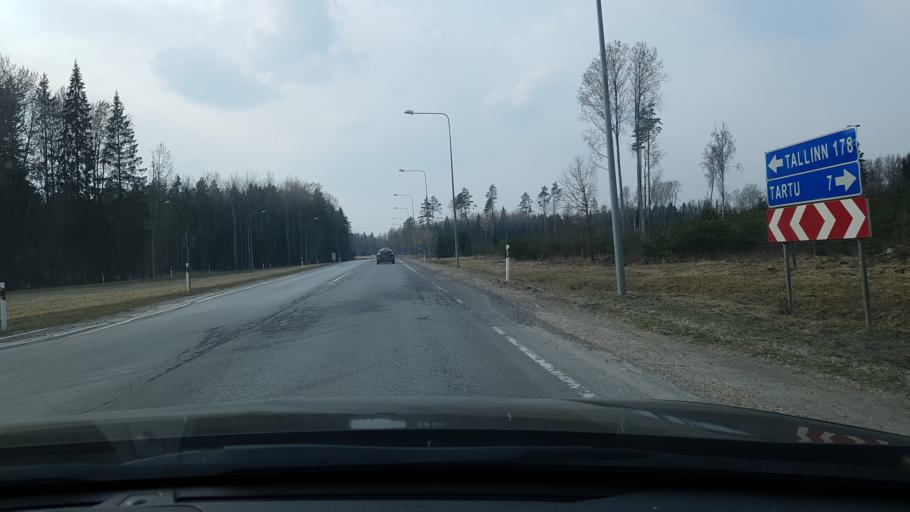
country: EE
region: Tartu
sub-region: Tartu linn
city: Tartu
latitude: 58.4091
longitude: 26.6503
